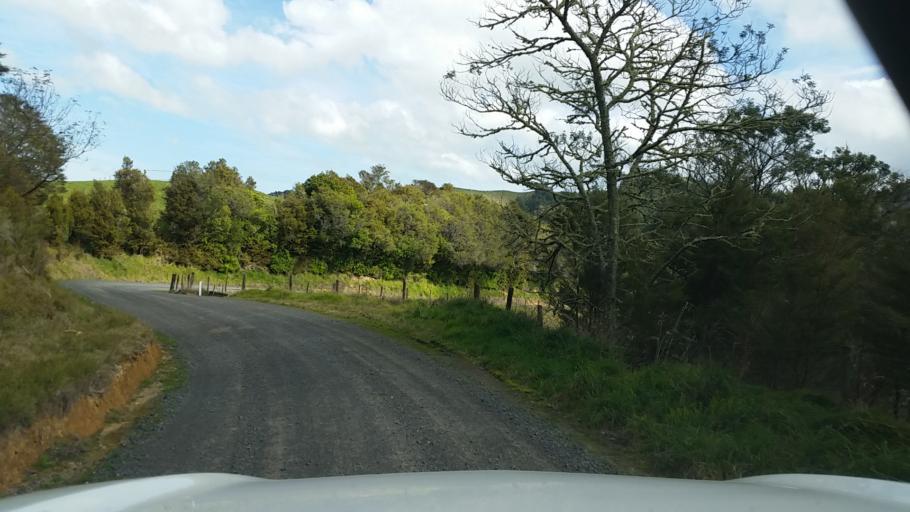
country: NZ
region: Waikato
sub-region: Hauraki District
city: Ngatea
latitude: -37.4656
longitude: 175.4610
